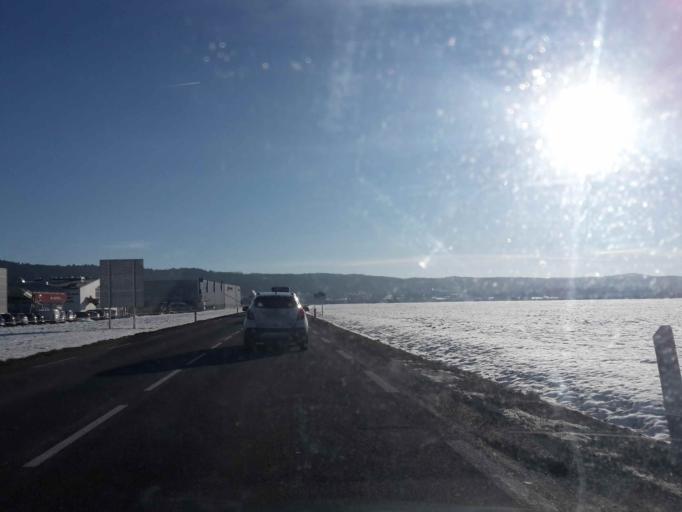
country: FR
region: Franche-Comte
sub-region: Departement du Doubs
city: Pontarlier
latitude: 46.9081
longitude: 6.3315
